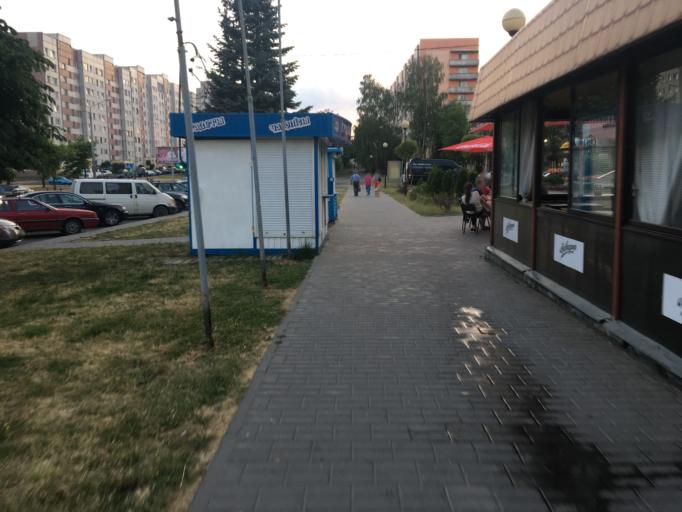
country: BY
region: Grodnenskaya
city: Hrodna
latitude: 53.7013
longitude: 23.8459
